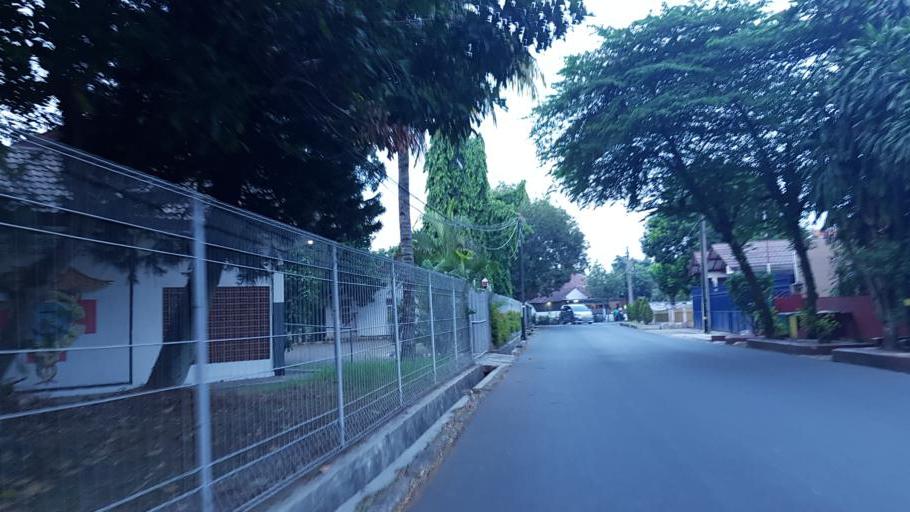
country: ID
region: West Java
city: Pamulang
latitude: -6.3135
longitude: 106.7838
